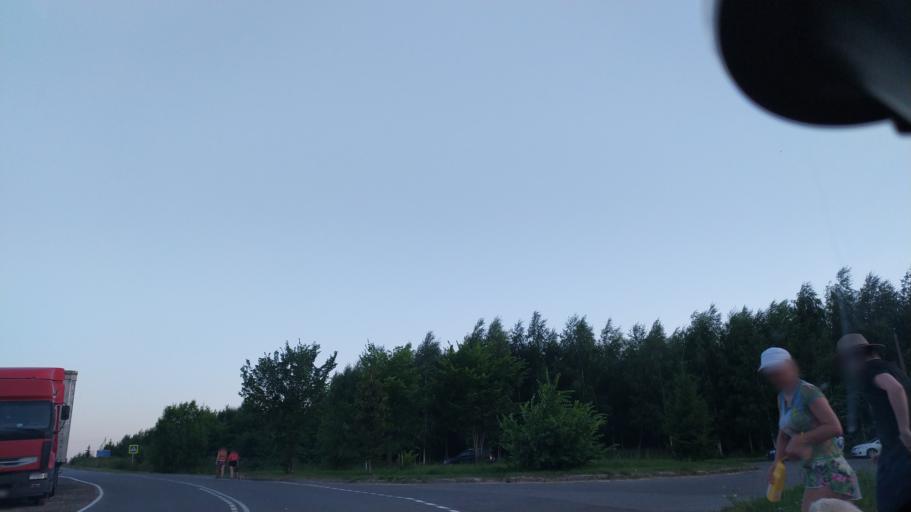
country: RU
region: Chuvashia
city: Ishley
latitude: 56.1244
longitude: 47.0407
